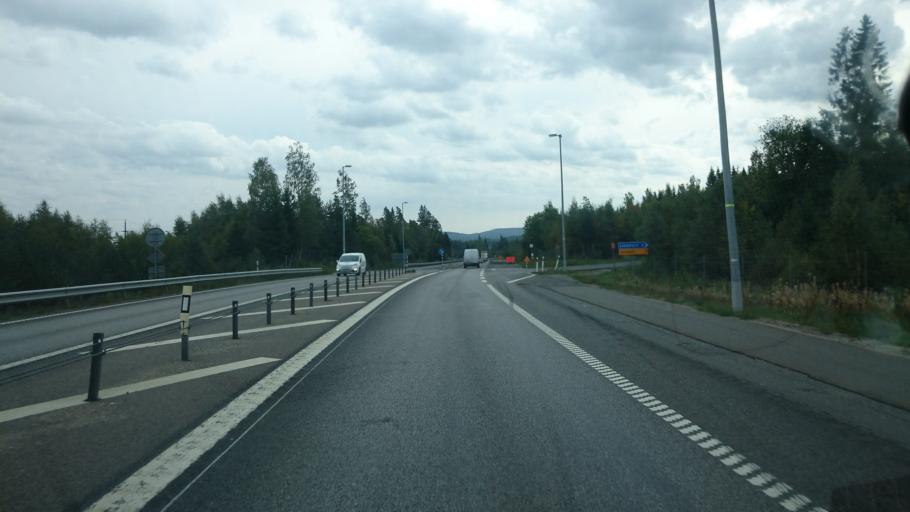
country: SE
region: Vaestra Goetaland
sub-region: Boras Kommun
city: Dalsjofors
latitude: 57.6351
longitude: 13.0813
